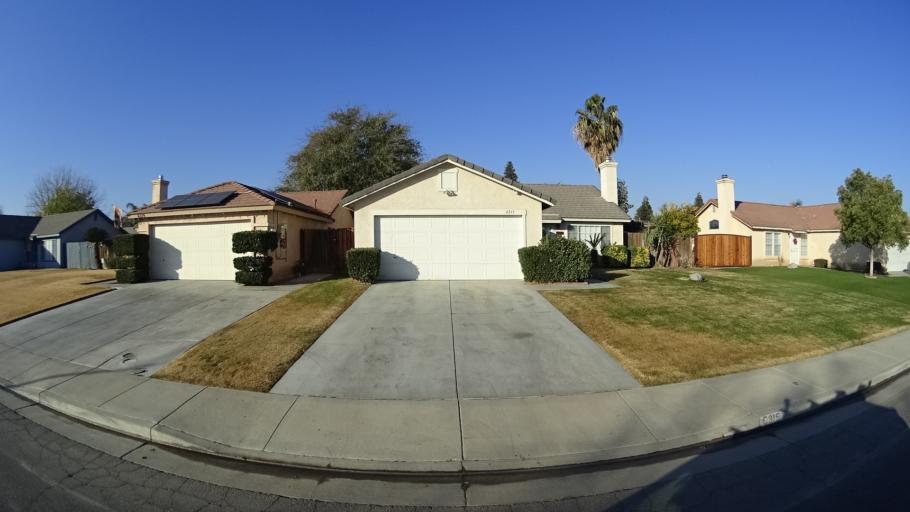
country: US
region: California
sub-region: Kern County
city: Greenfield
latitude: 35.2976
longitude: -119.0090
